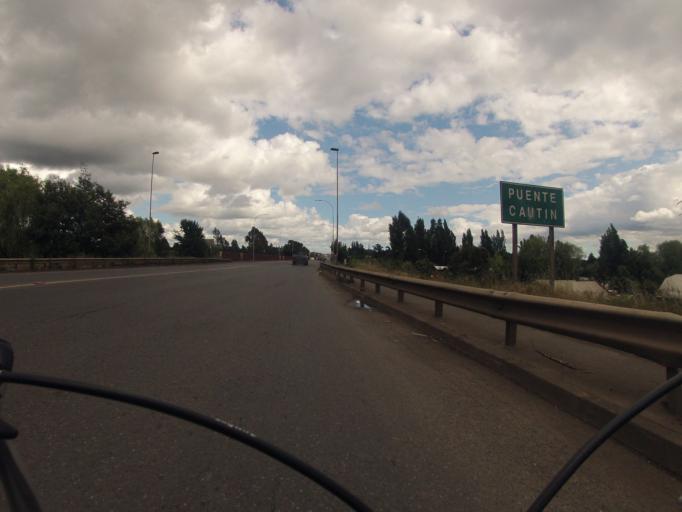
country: CL
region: Araucania
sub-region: Provincia de Cautin
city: Temuco
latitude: -38.7546
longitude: -72.6093
